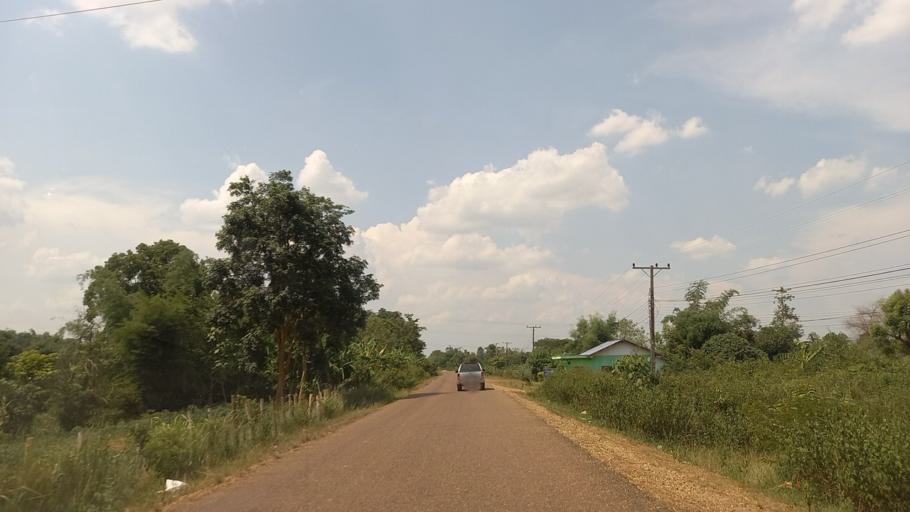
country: LA
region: Bolikhamxai
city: Muang Pakxan
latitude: 18.4092
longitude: 103.7022
